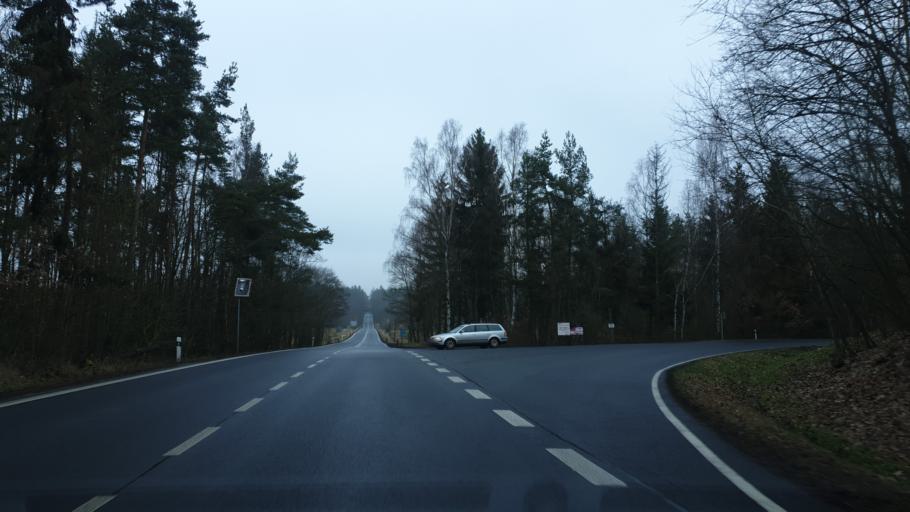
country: CZ
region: Karlovarsky
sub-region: Okres Cheb
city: Frantiskovy Lazne
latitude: 50.1403
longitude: 12.3350
